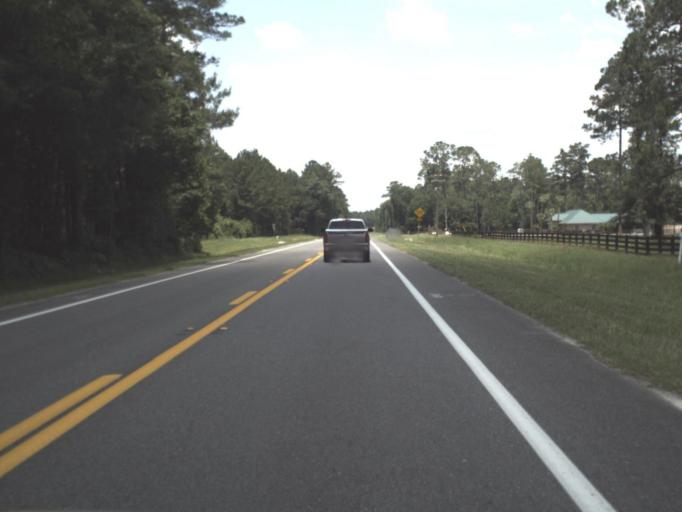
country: US
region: Florida
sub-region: Union County
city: Lake Butler
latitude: 30.0538
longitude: -82.4106
